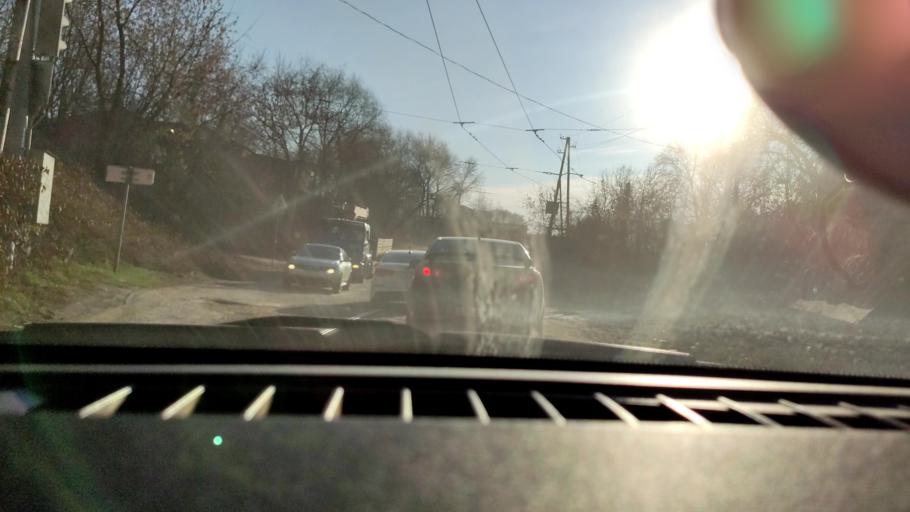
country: RU
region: Perm
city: Kondratovo
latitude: 58.0049
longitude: 56.1631
